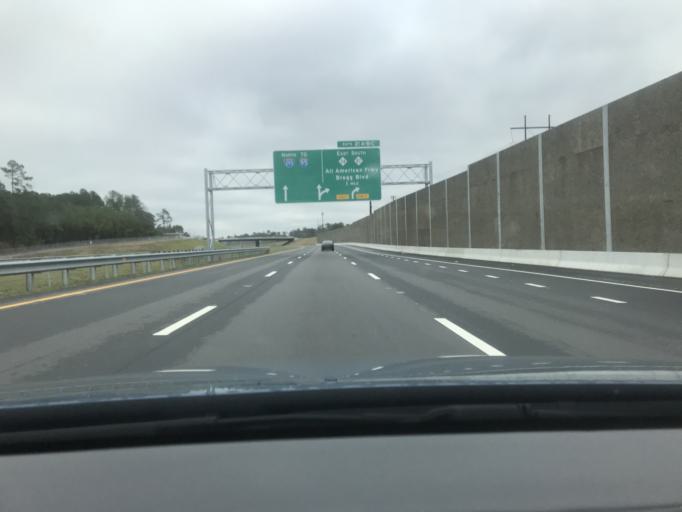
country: US
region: North Carolina
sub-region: Cumberland County
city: Fort Bragg
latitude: 35.1071
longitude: -79.0024
